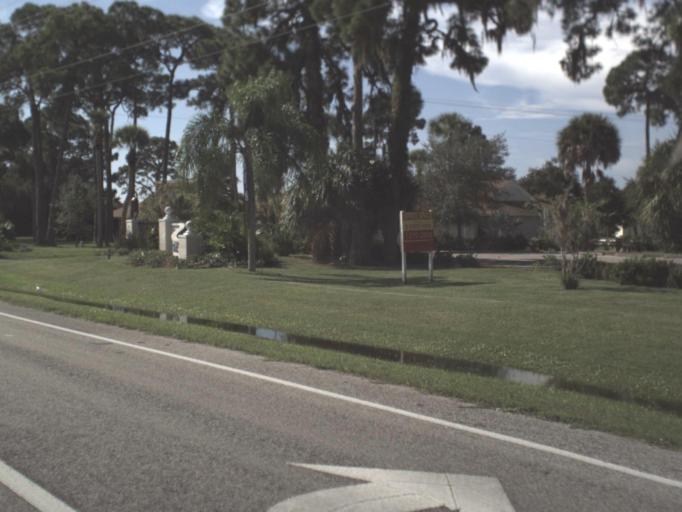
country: US
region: Florida
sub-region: Sarasota County
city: Laurel
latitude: 27.1618
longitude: -82.4735
